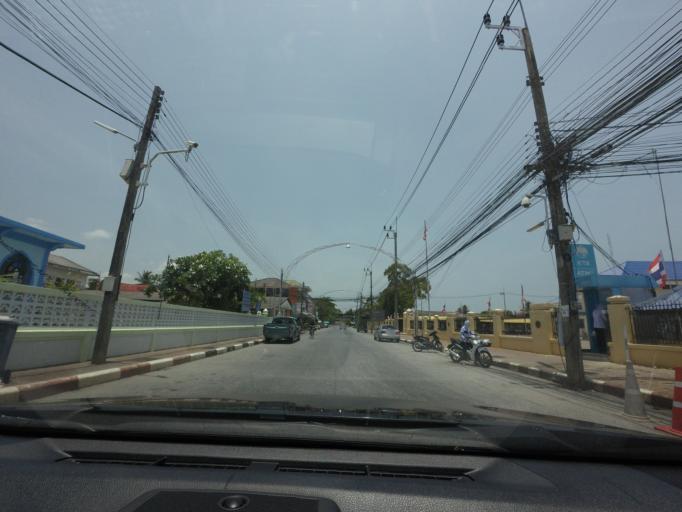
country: TH
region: Pattani
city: Yaring
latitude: 6.8657
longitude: 101.3692
